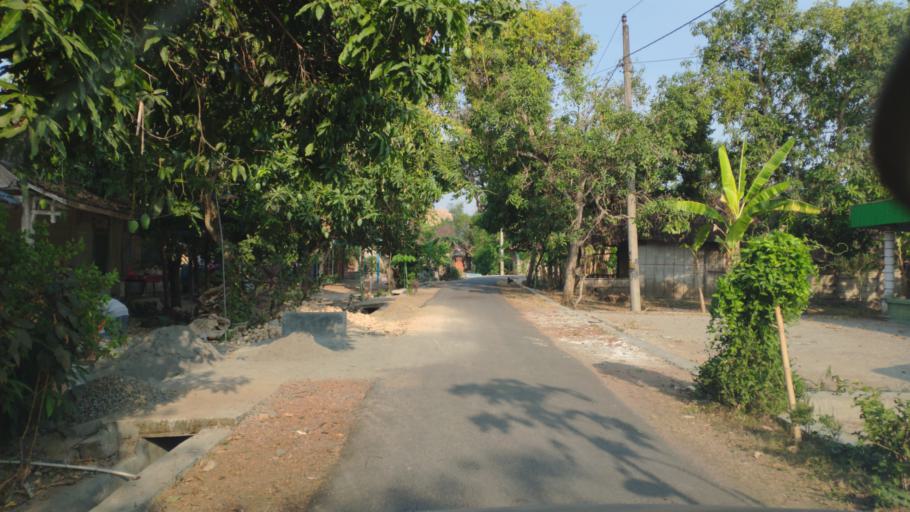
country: ID
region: Central Java
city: Ngampon
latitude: -7.0080
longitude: 111.4275
